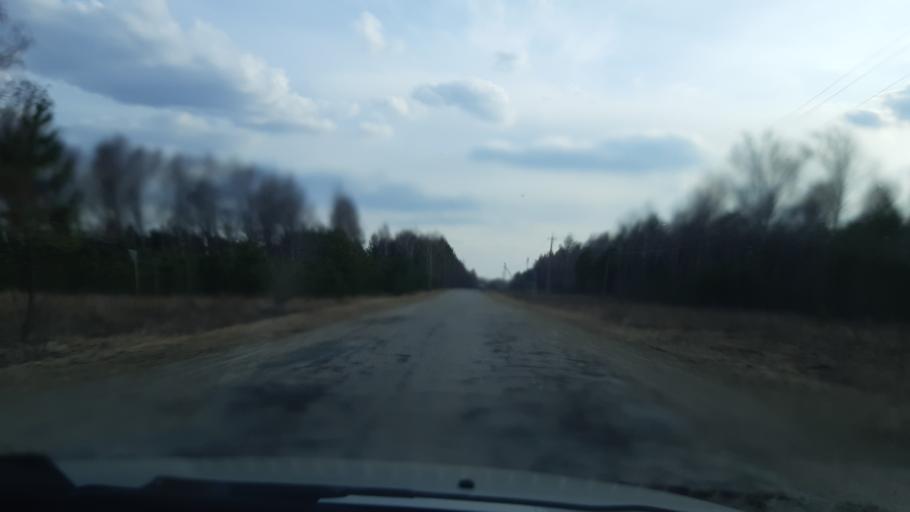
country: RU
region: Vladimir
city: Nikologory
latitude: 56.1156
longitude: 41.9850
